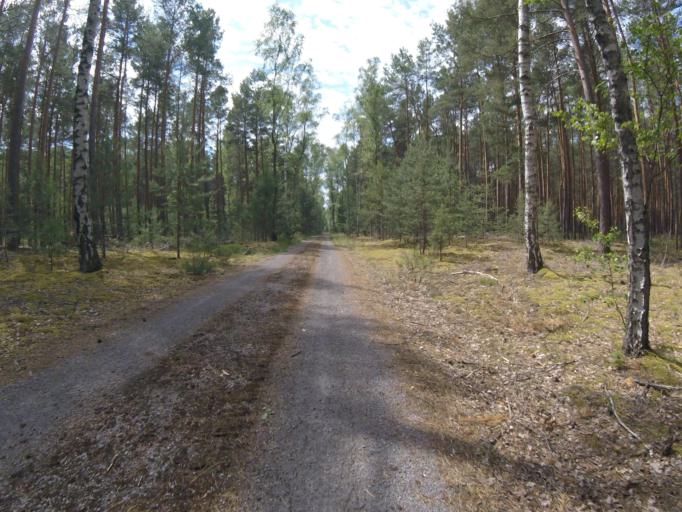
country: DE
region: Brandenburg
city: Halbe
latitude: 52.1231
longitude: 13.6706
